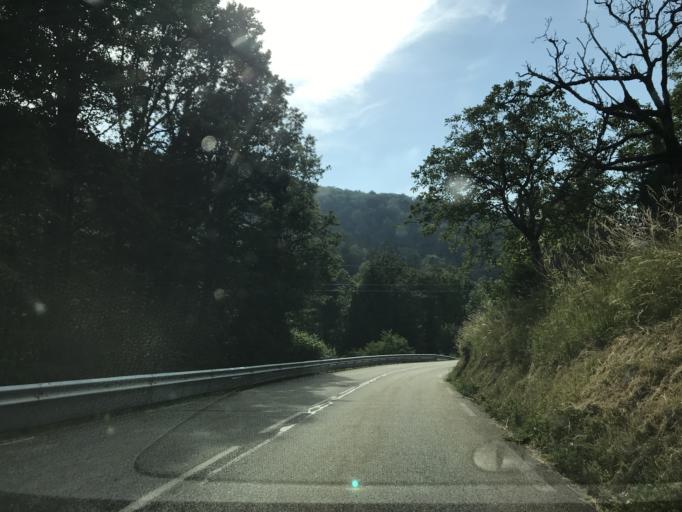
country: FR
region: Rhone-Alpes
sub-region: Departement de l'Isere
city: Allevard
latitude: 45.3808
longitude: 6.0884
